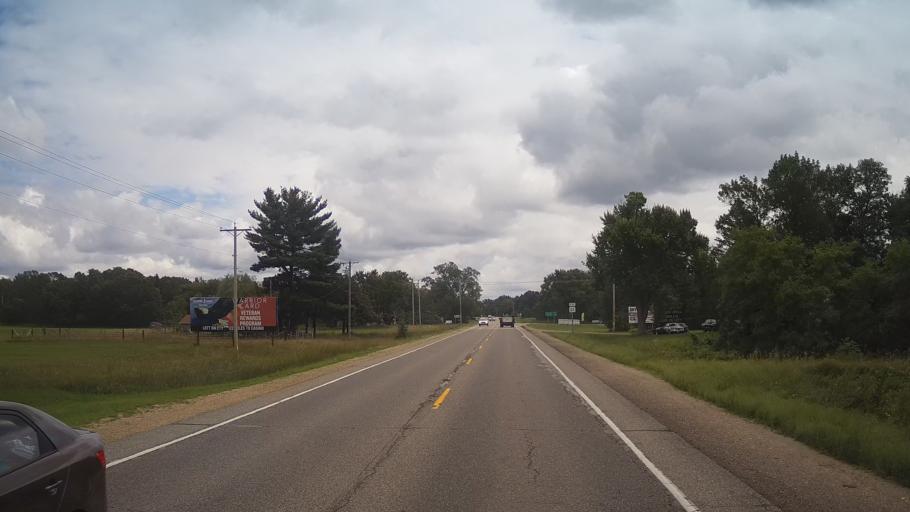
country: US
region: Wisconsin
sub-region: Juneau County
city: New Lisbon
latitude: 44.0276
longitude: -90.0631
